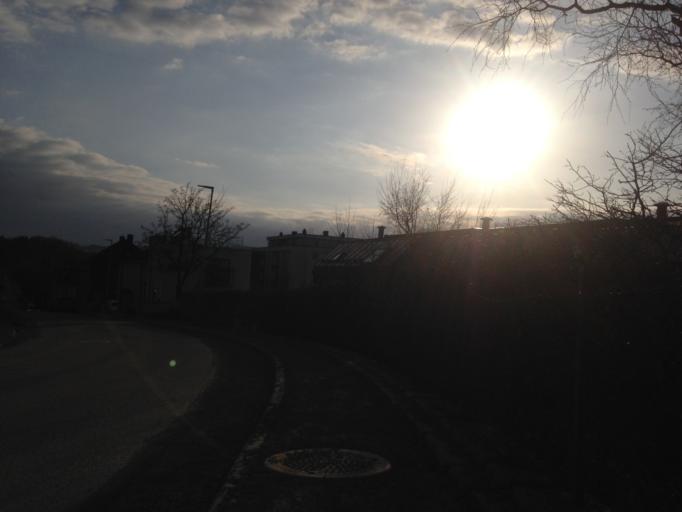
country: NO
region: Sor-Trondelag
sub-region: Trondheim
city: Trondheim
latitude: 63.4341
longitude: 10.4219
